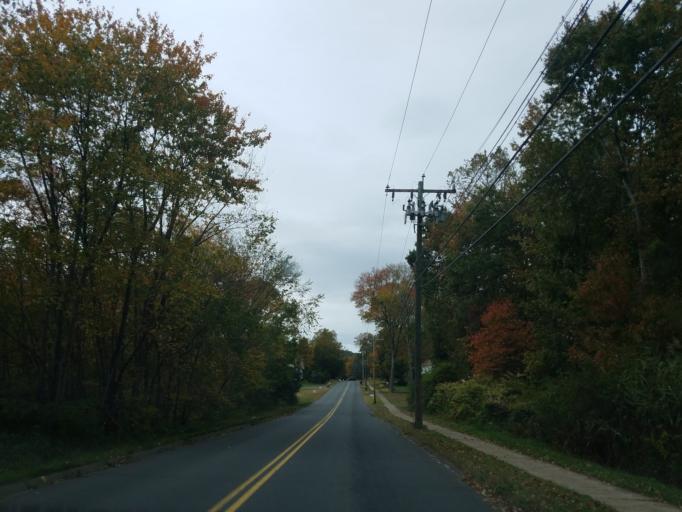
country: US
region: Connecticut
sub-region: New Haven County
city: Cheshire
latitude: 41.4993
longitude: -72.9178
